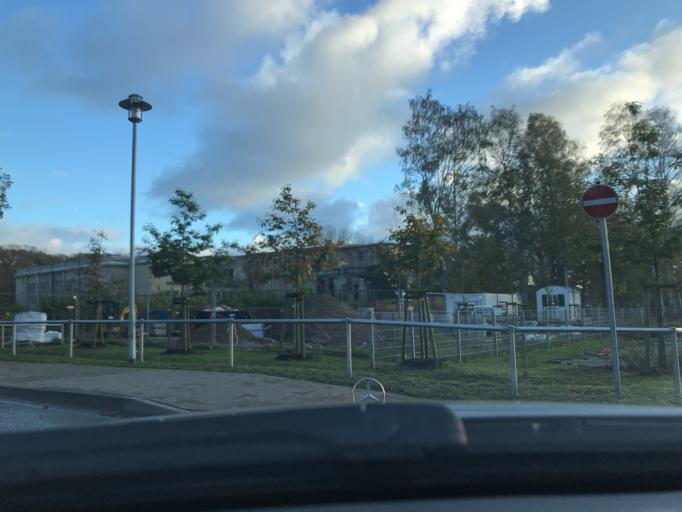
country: DE
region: Mecklenburg-Vorpommern
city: Ostseebad Zinnowitz
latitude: 54.0808
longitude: 13.9095
